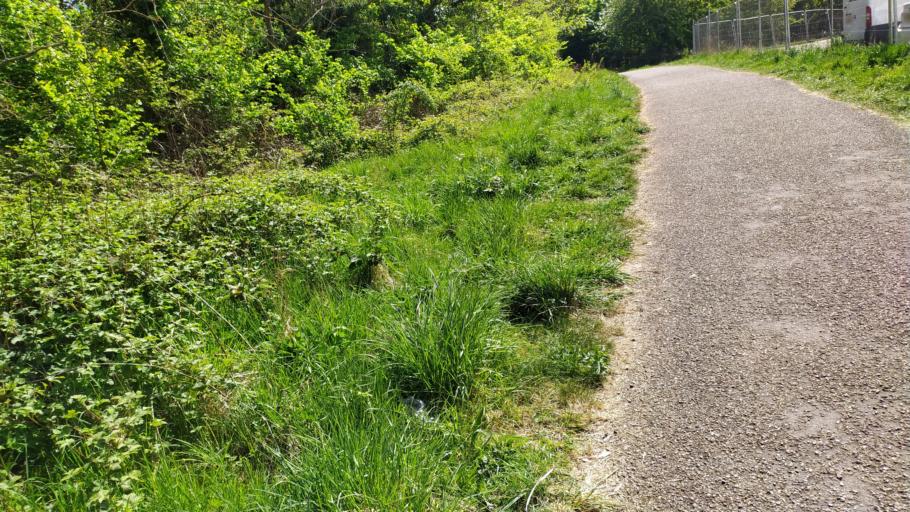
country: GB
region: England
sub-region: City and Borough of Leeds
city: Shadwell
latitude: 53.8063
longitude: -1.4837
